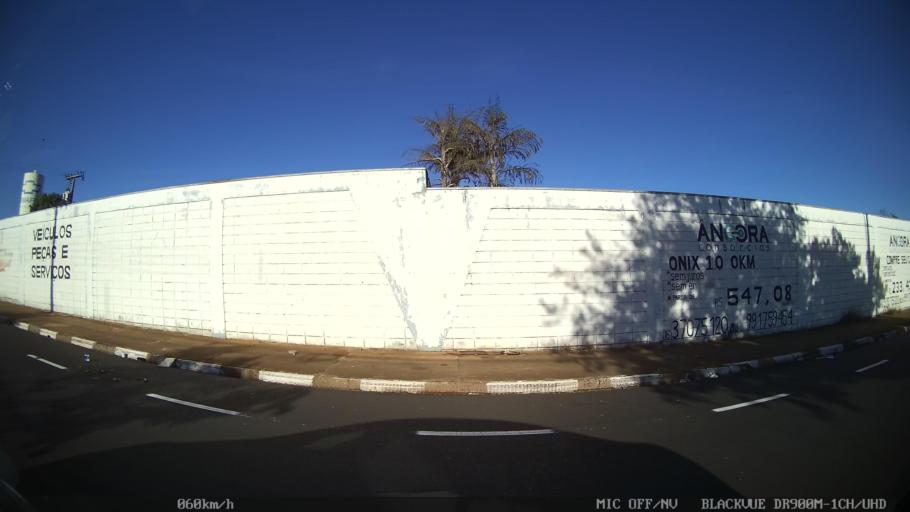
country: BR
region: Sao Paulo
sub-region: Franca
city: Franca
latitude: -20.5686
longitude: -47.3945
